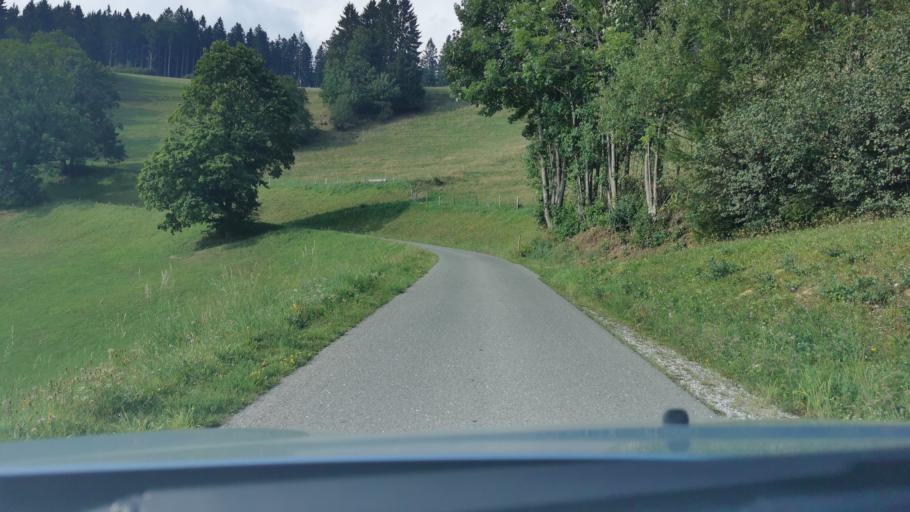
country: AT
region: Styria
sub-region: Politischer Bezirk Weiz
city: Fischbach
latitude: 47.4031
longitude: 15.6204
